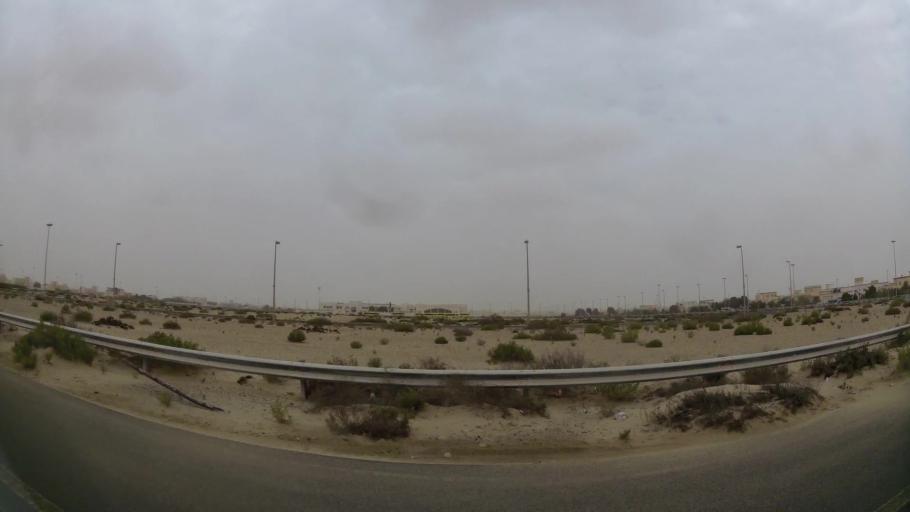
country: AE
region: Abu Dhabi
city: Abu Dhabi
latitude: 24.3904
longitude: 54.7414
